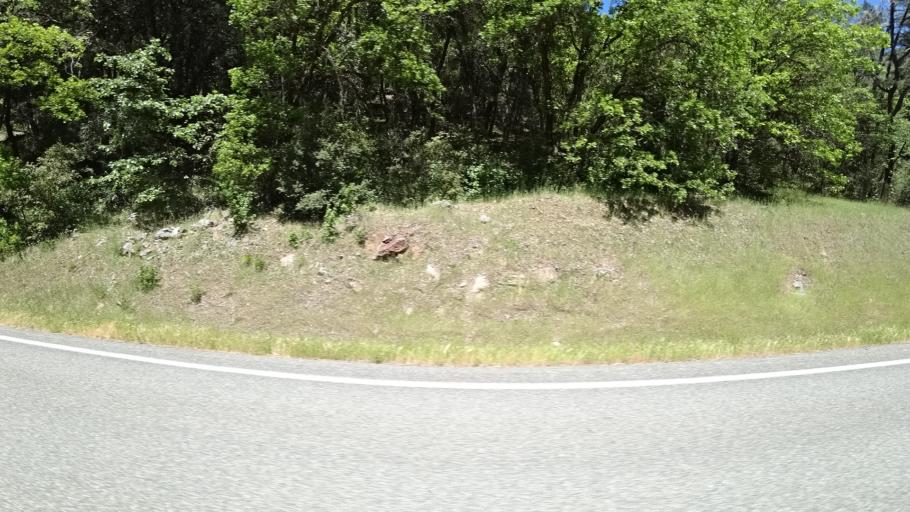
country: US
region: California
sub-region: Trinity County
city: Hayfork
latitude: 40.7384
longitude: -123.2363
